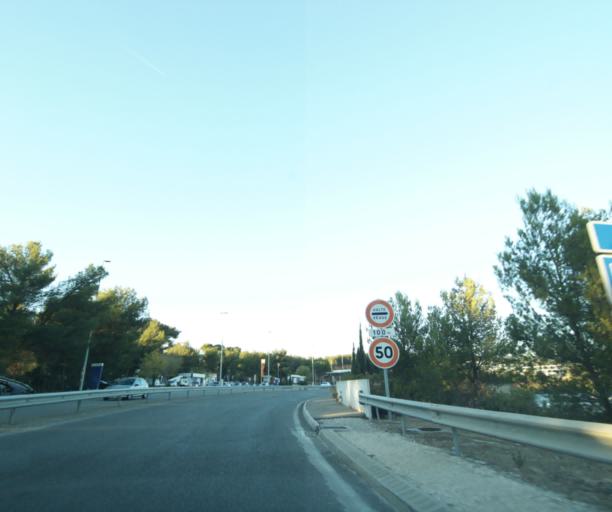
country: FR
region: Provence-Alpes-Cote d'Azur
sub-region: Departement des Bouches-du-Rhone
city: La Ciotat
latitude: 43.2007
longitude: 5.5942
